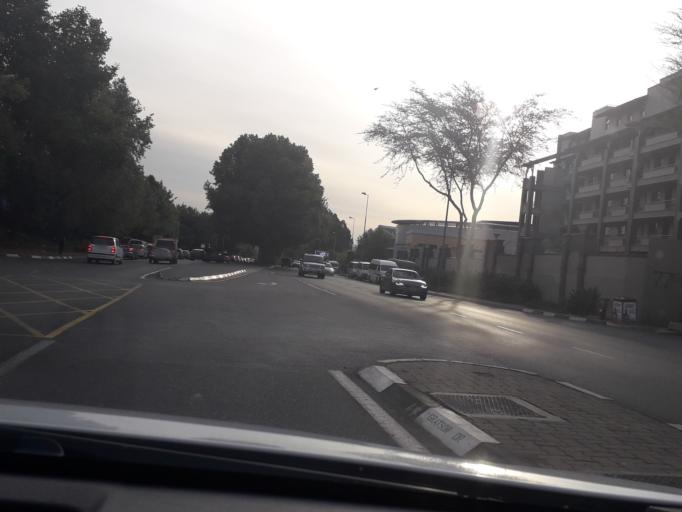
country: ZA
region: Gauteng
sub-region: City of Johannesburg Metropolitan Municipality
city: Johannesburg
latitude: -26.1000
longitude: 28.0524
